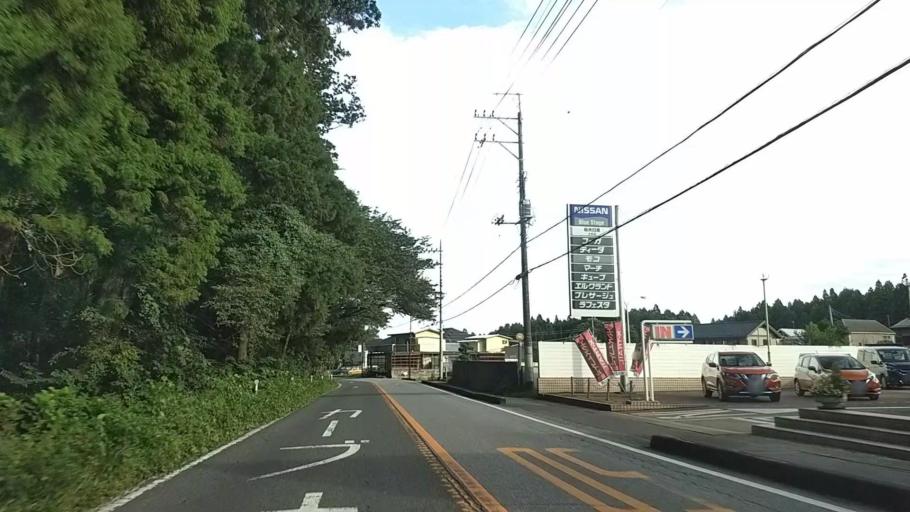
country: JP
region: Tochigi
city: Imaichi
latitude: 36.7188
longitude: 139.7111
